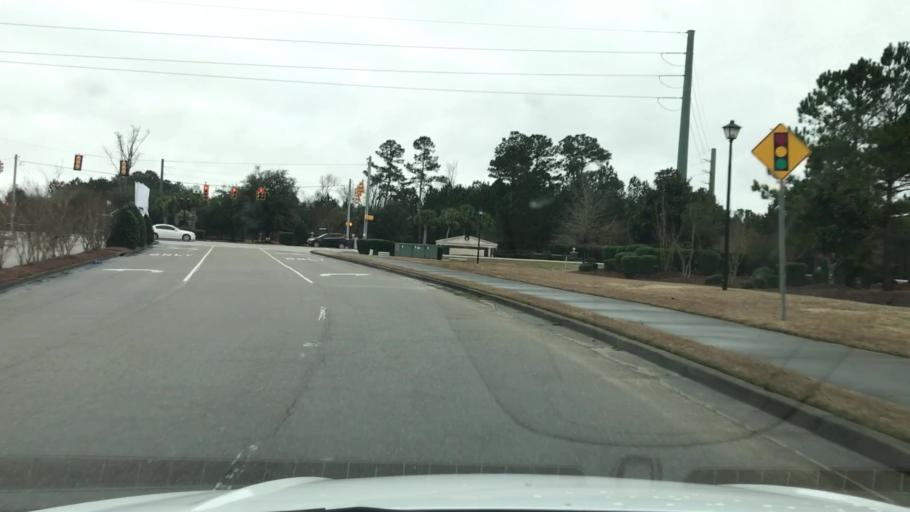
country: US
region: South Carolina
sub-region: Horry County
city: Myrtle Beach
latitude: 33.7375
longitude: -78.8972
